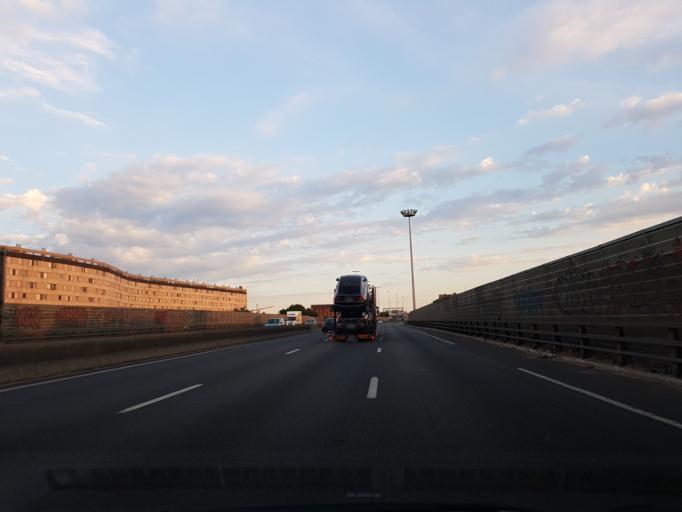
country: FR
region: Ile-de-France
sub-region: Departement de Seine-Saint-Denis
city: Noisy-le-Sec
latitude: 48.9051
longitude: 2.4717
